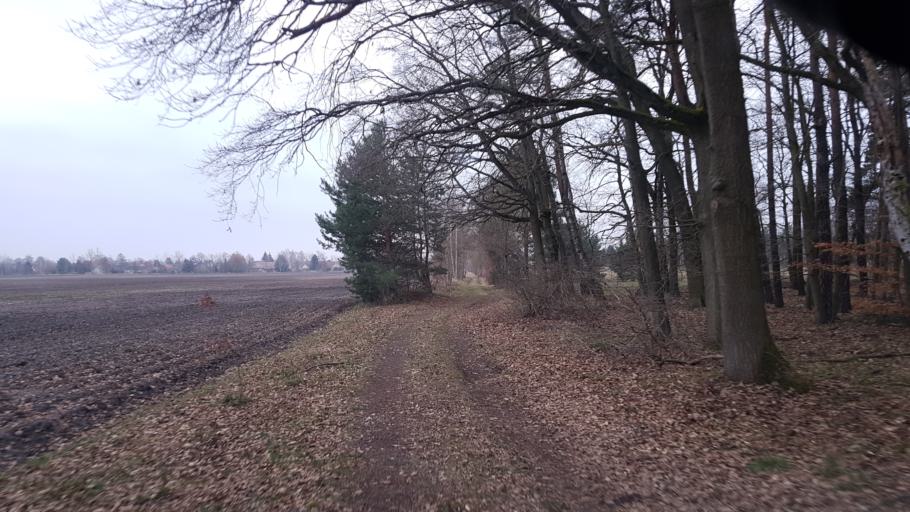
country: DE
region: Brandenburg
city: Schonborn
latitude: 51.6023
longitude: 13.5002
